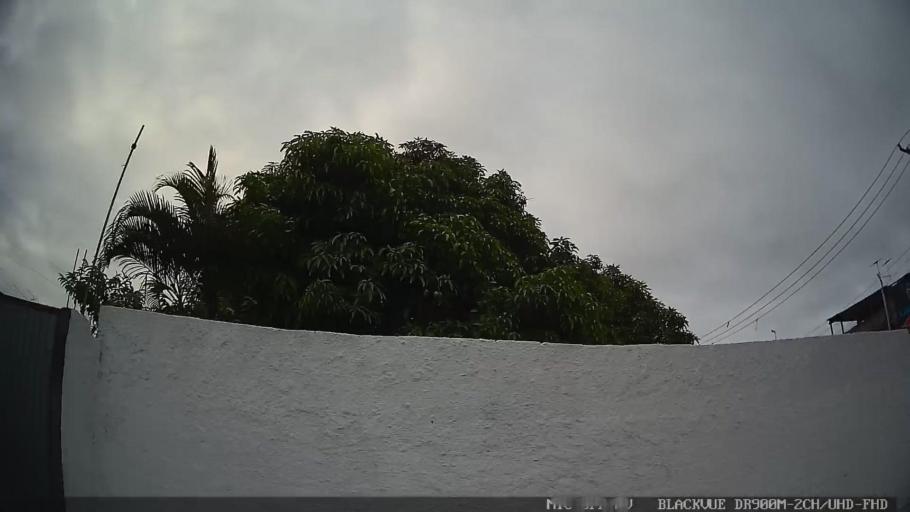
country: BR
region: Sao Paulo
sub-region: Itaquaquecetuba
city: Itaquaquecetuba
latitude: -23.4877
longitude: -46.3913
